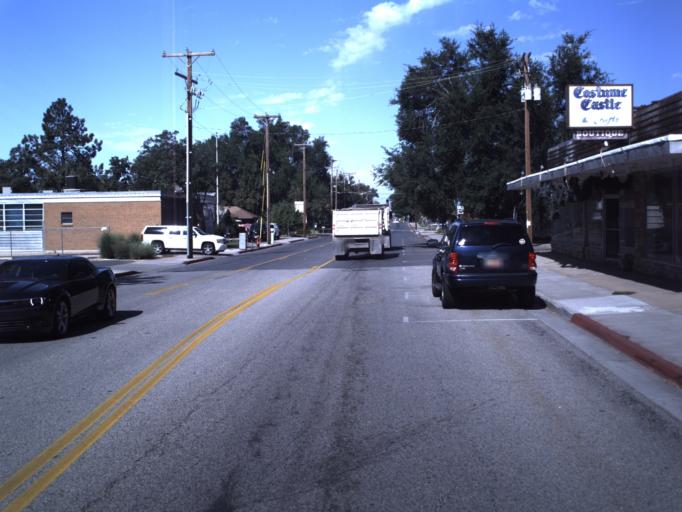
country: US
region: Utah
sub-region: Davis County
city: Layton
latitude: 41.0602
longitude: -111.9671
